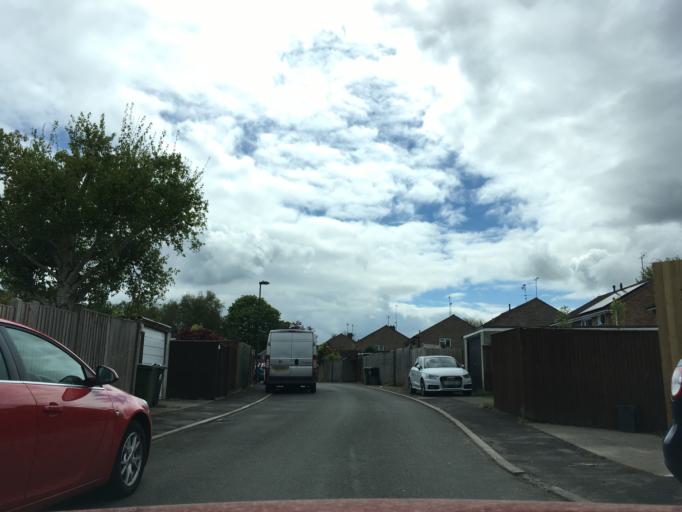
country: GB
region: England
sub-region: South Gloucestershire
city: Thornbury
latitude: 51.6173
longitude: -2.5225
